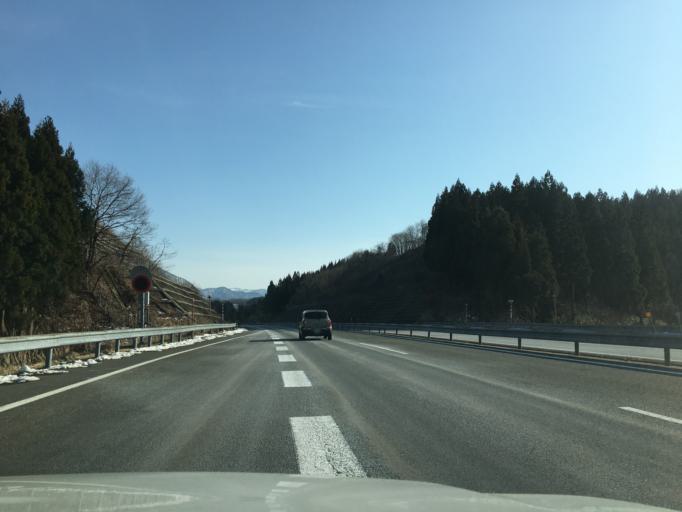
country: JP
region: Yamagata
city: Tsuruoka
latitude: 38.6406
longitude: 139.8298
